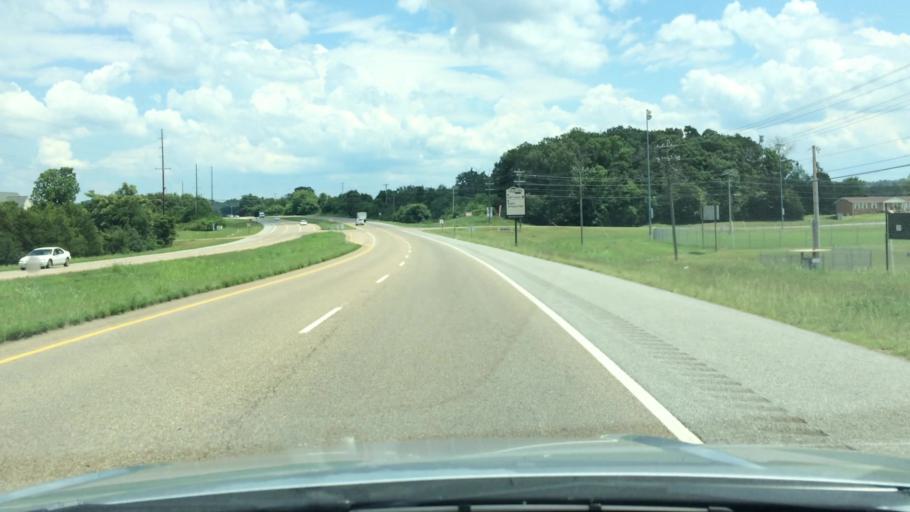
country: US
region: Tennessee
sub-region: Hamblen County
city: Morristown
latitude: 36.1669
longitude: -83.3783
